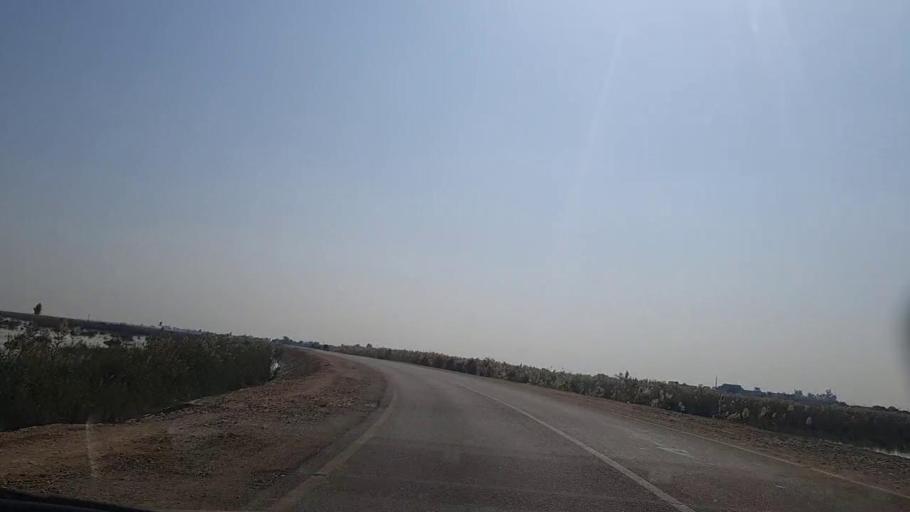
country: PK
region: Sindh
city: Sakrand
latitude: 26.0814
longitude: 68.4026
